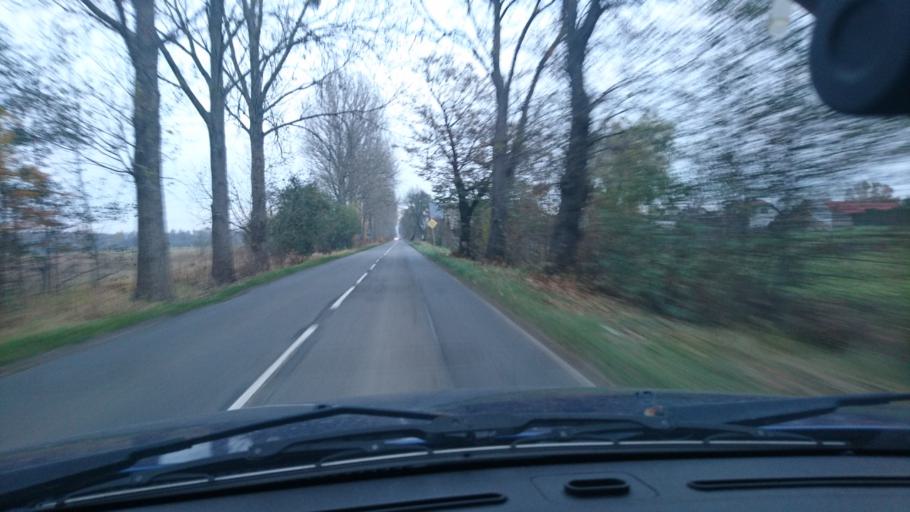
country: PL
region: Greater Poland Voivodeship
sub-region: Powiat ostrowski
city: Odolanow
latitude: 51.5442
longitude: 17.6553
